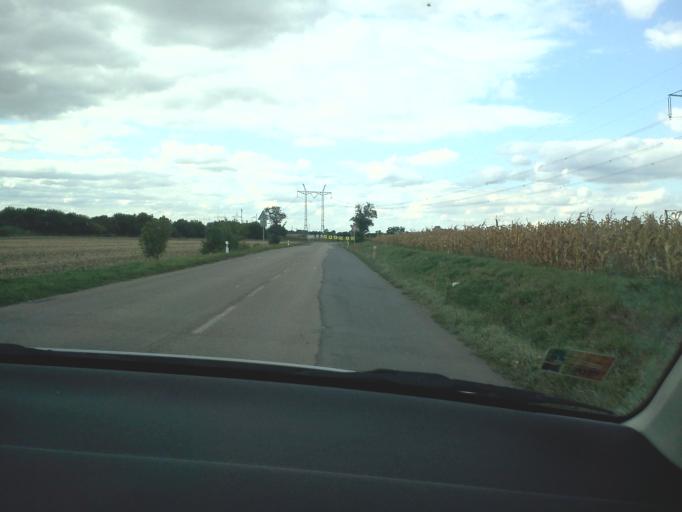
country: CZ
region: Central Bohemia
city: Cesky Brod
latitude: 50.1154
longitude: 14.8611
